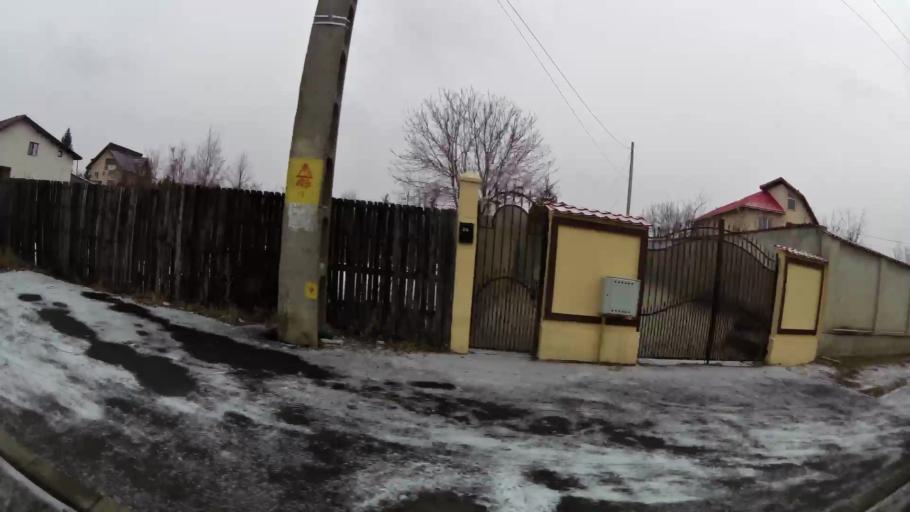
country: RO
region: Dambovita
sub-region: Municipiul Targoviste
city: Targoviste
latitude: 44.9372
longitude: 25.4691
